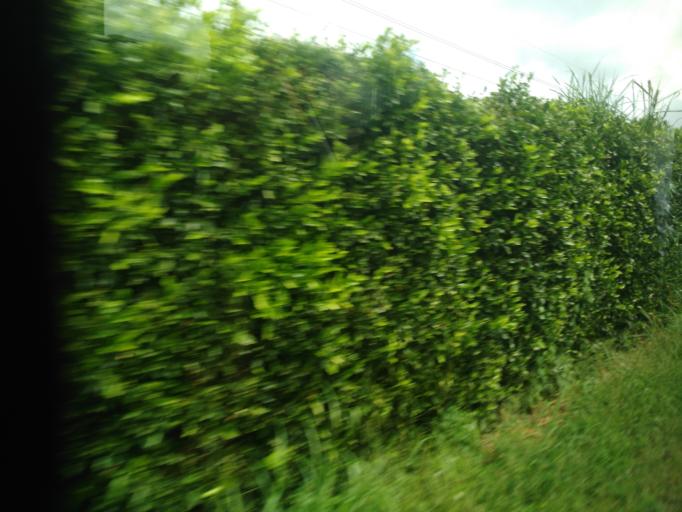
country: CO
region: Valle del Cauca
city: Caicedonia
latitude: 4.3221
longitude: -75.8722
